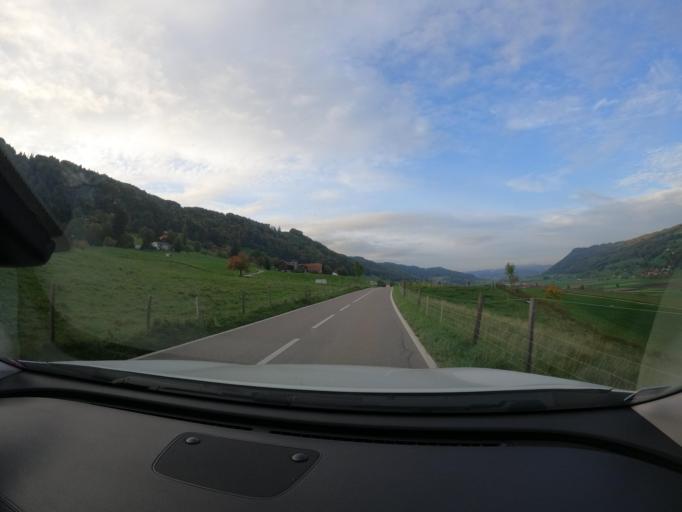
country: CH
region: Bern
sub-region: Bern-Mittelland District
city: Toffen
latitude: 46.8439
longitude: 7.4924
